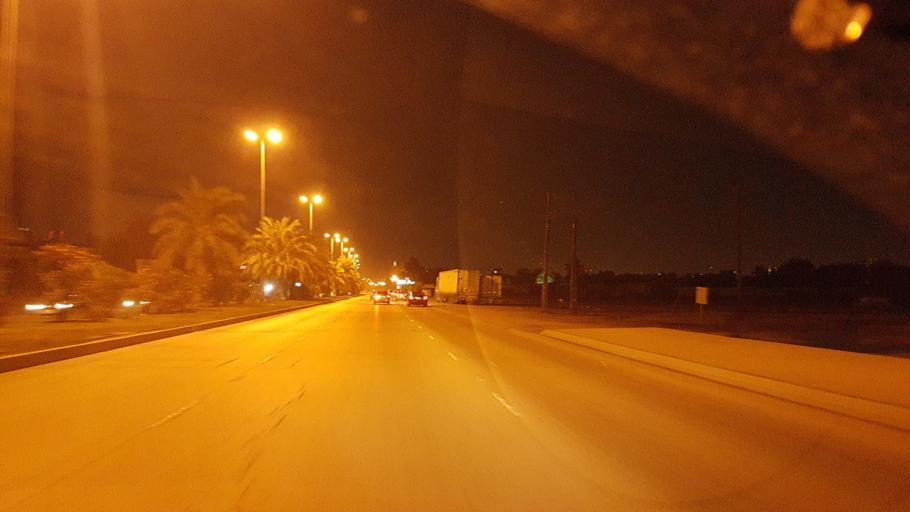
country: BH
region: Manama
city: Jidd Hafs
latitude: 26.2214
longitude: 50.5543
